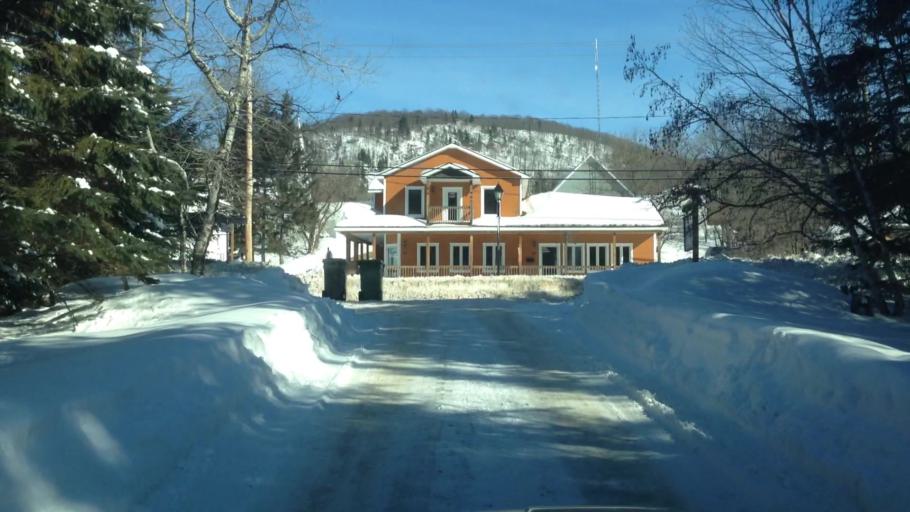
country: CA
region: Quebec
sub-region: Laurentides
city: Mont-Tremblant
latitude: 45.9440
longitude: -74.5479
